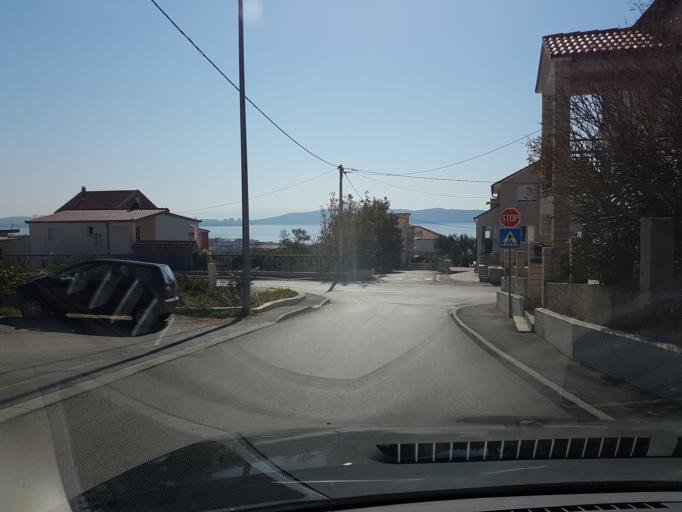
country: HR
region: Splitsko-Dalmatinska
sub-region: Grad Split
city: Split
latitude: 43.5585
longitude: 16.3865
